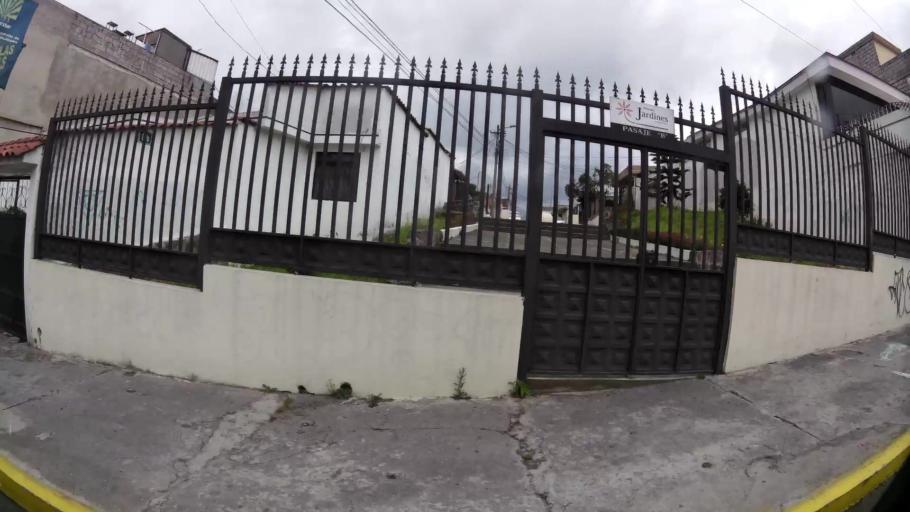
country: EC
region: Pichincha
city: Quito
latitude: -0.1196
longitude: -78.5018
